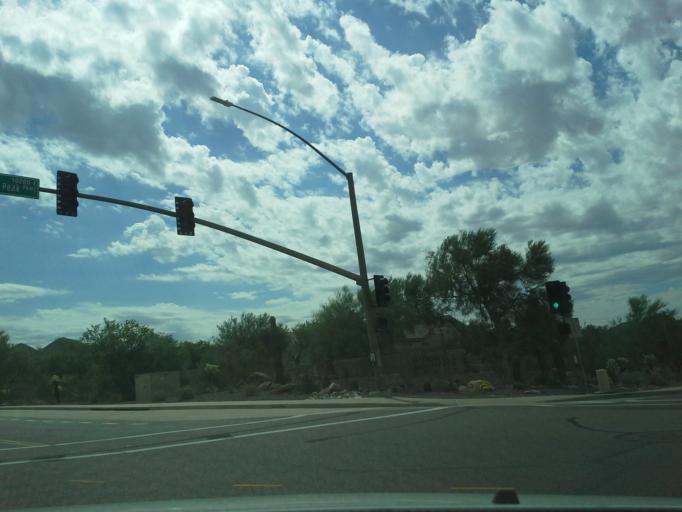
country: US
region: Arizona
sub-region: Maricopa County
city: Paradise Valley
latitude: 33.6401
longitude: -111.8611
